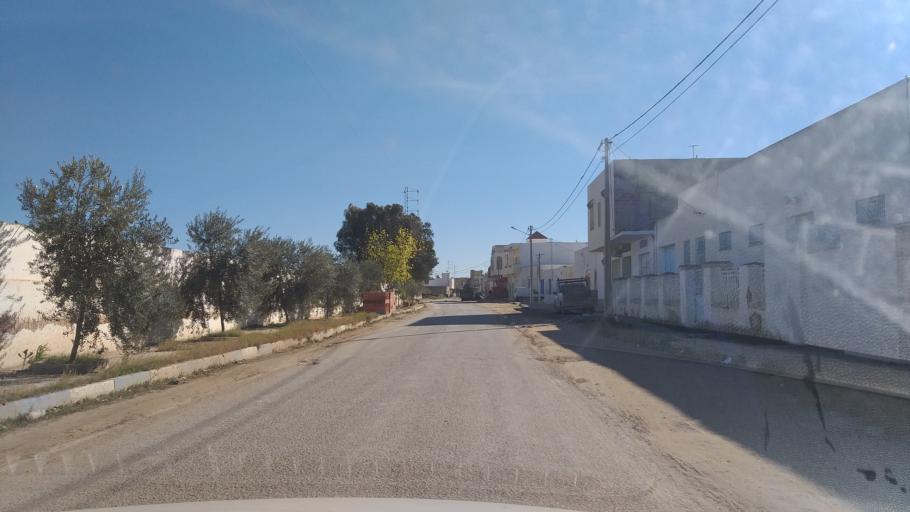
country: TN
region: Al Mahdiyah
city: El Jem
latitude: 35.2944
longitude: 10.7136
